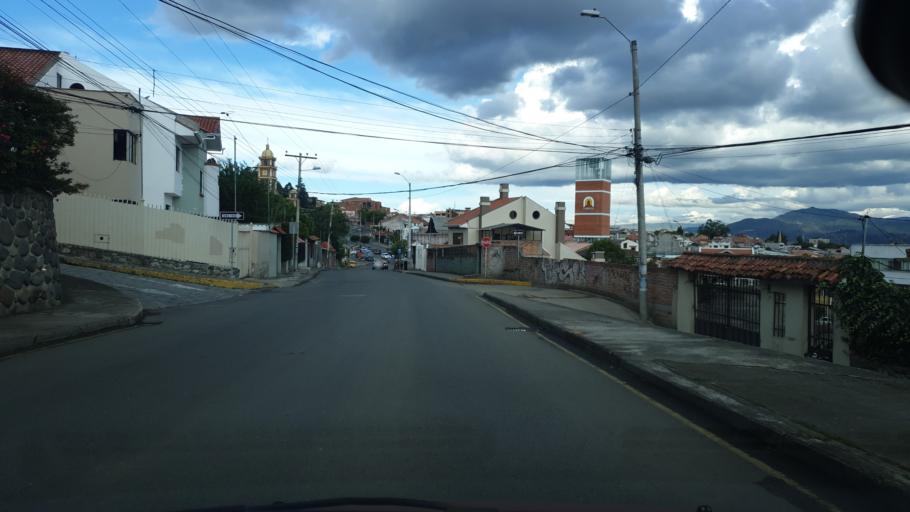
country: EC
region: Azuay
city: Cuenca
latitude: -2.8871
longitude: -79.0103
